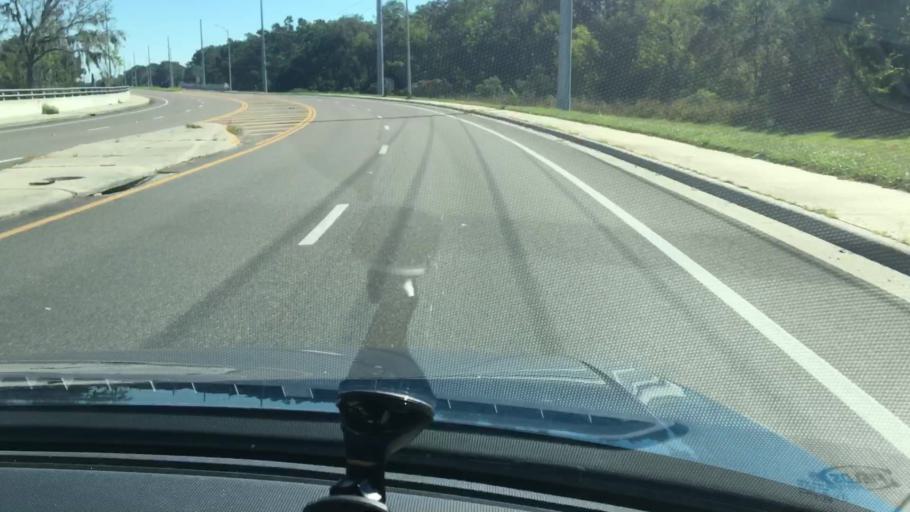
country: US
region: Florida
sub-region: Polk County
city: Kathleen
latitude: 28.1182
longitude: -82.0232
